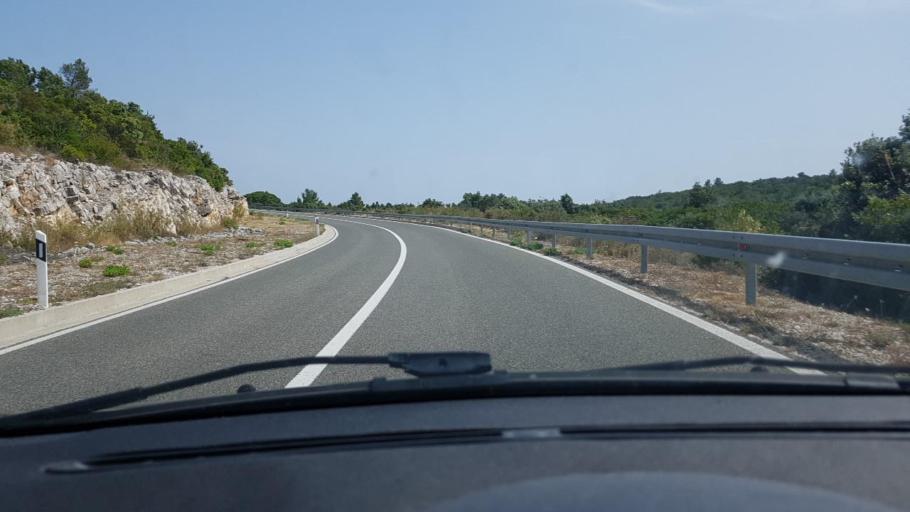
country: HR
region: Dubrovacko-Neretvanska
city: Smokvica
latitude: 42.9499
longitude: 16.9422
